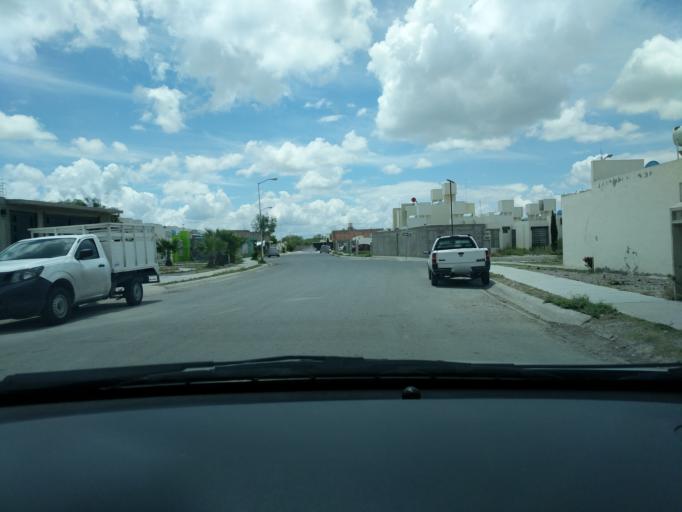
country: MX
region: San Luis Potosi
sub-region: San Luis Potosi
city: Fraccion Milpillas
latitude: 22.2185
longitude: -100.9346
